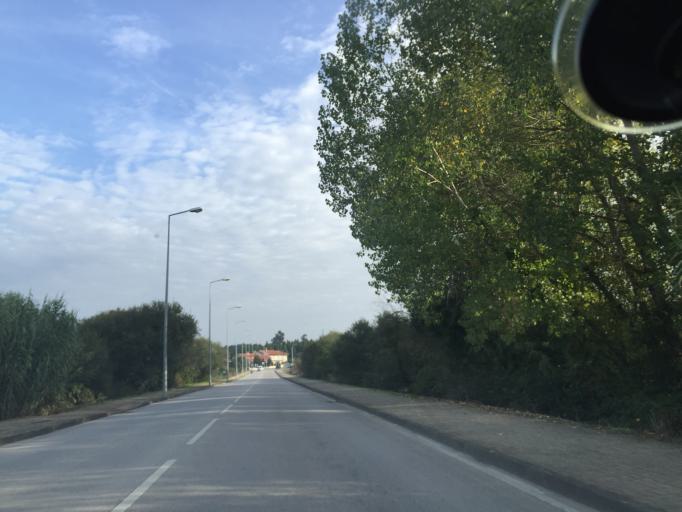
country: PT
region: Aveiro
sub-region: Anadia
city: Arcos
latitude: 40.4508
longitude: -8.4355
